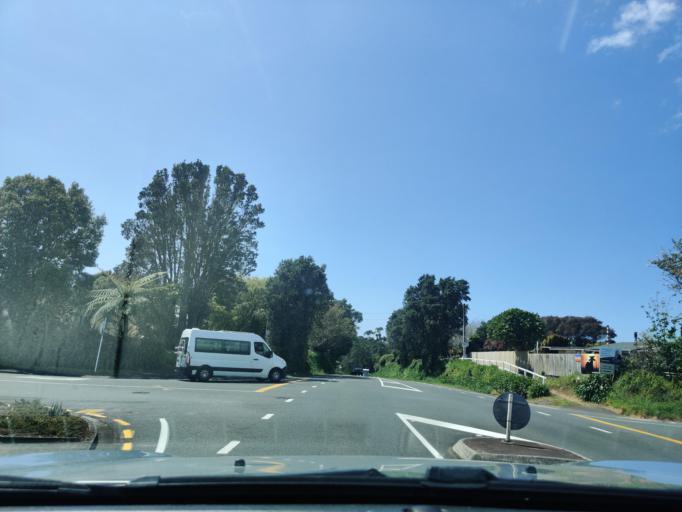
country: NZ
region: Taranaki
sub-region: New Plymouth District
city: New Plymouth
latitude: -39.1155
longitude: 173.9573
